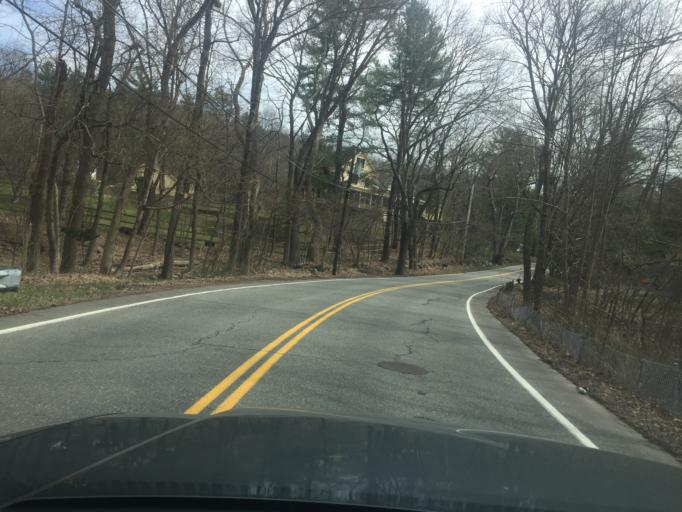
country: US
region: Massachusetts
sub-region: Norfolk County
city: Medfield
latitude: 42.2106
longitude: -71.3131
